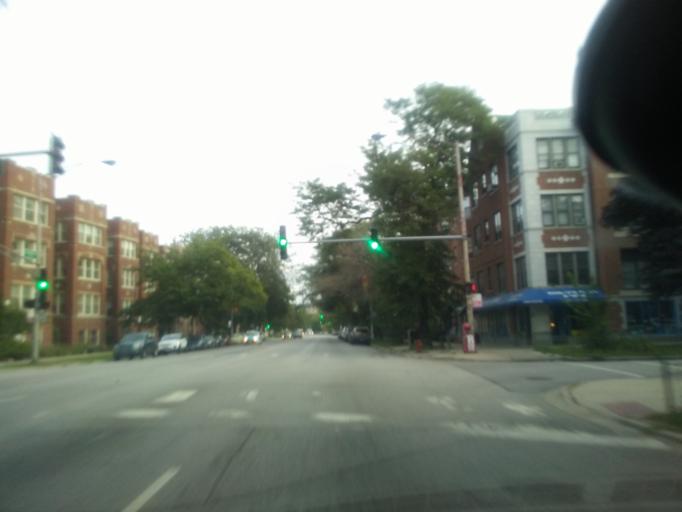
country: US
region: Illinois
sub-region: Cook County
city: Evanston
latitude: 42.0091
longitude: -87.6620
